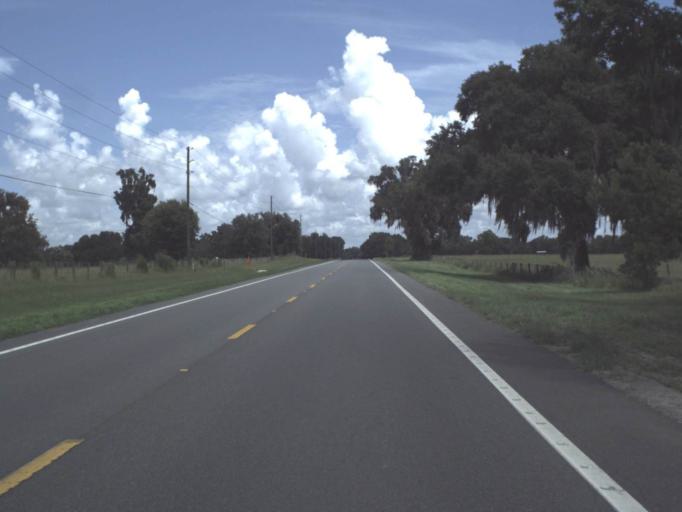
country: US
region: Florida
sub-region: Alachua County
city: Archer
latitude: 29.5065
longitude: -82.4065
